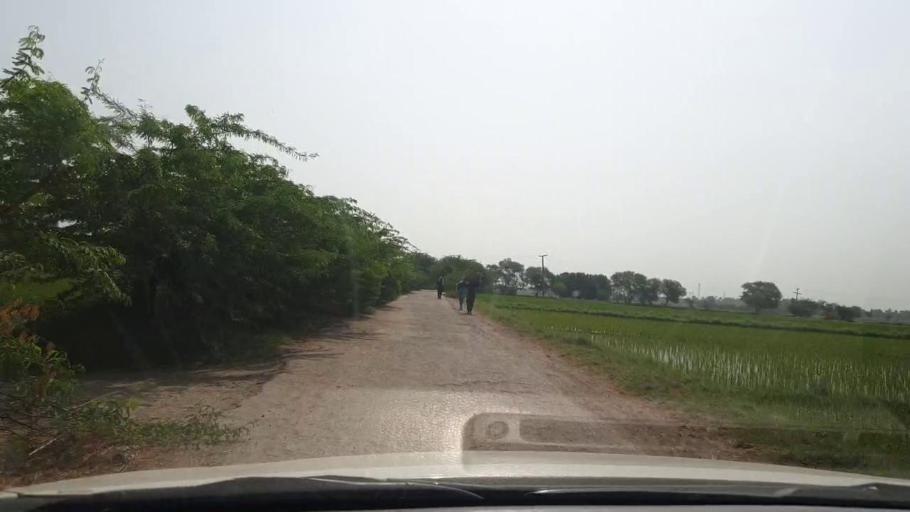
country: PK
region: Sindh
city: Shikarpur
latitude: 27.9839
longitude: 68.6705
